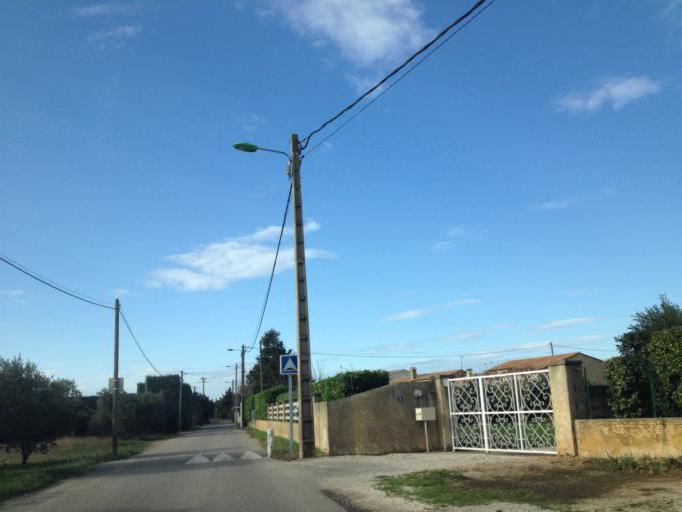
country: FR
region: Provence-Alpes-Cote d'Azur
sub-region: Departement du Vaucluse
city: Sorgues
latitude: 44.0333
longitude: 4.8702
